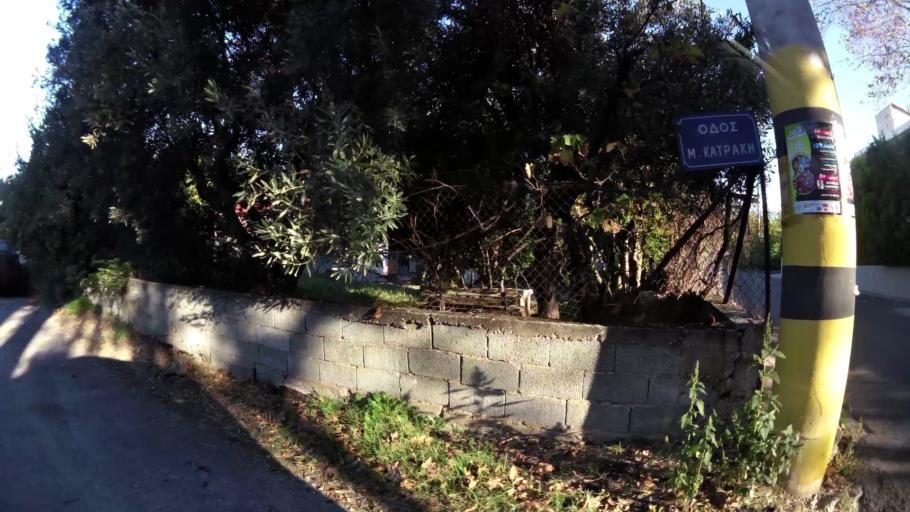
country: GR
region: Attica
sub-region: Nomarchia Anatolikis Attikis
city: Pallini
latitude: 38.0104
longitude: 23.8729
